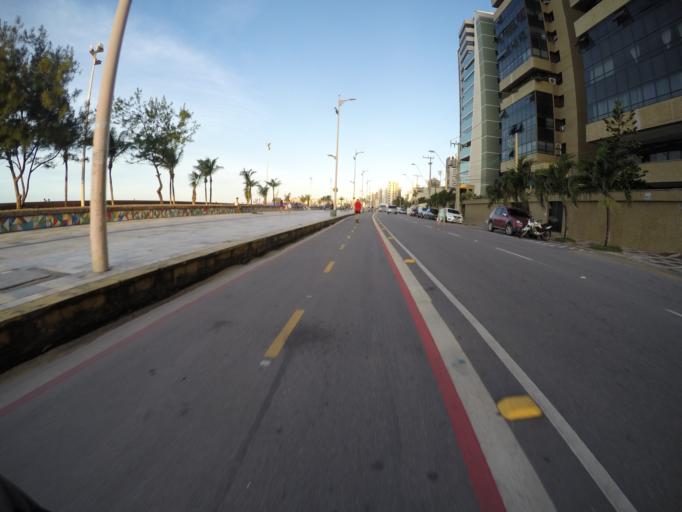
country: BR
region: Ceara
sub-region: Fortaleza
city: Fortaleza
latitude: -3.7206
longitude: -38.5107
